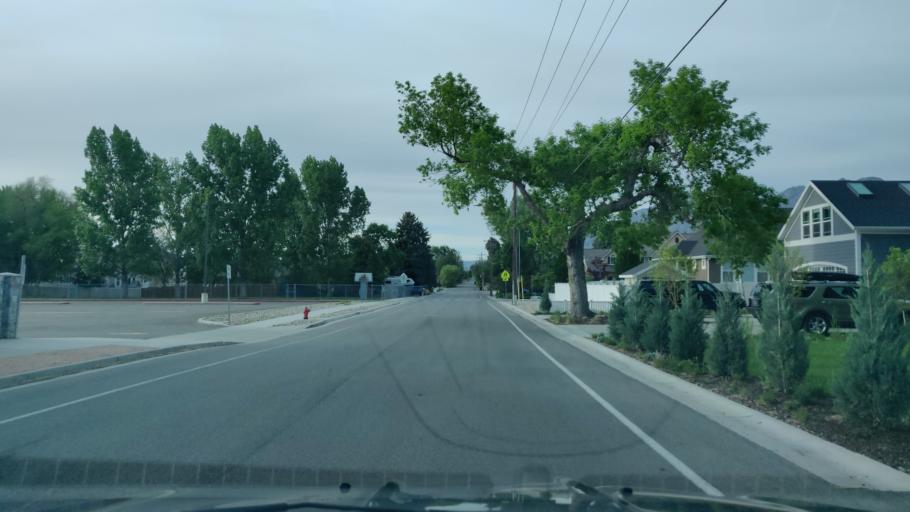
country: US
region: Utah
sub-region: Salt Lake County
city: Granite
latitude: 40.5738
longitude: -111.8056
